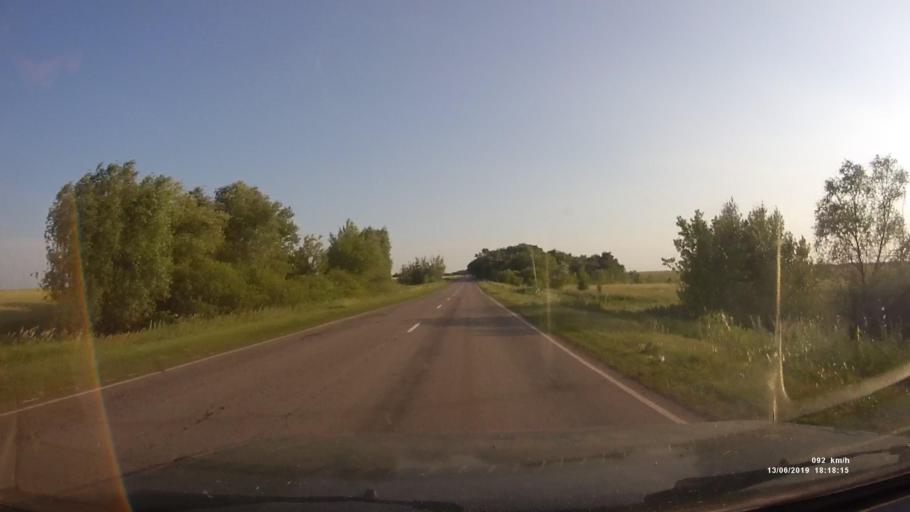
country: RU
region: Rostov
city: Kazanskaya
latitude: 49.9103
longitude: 41.3161
